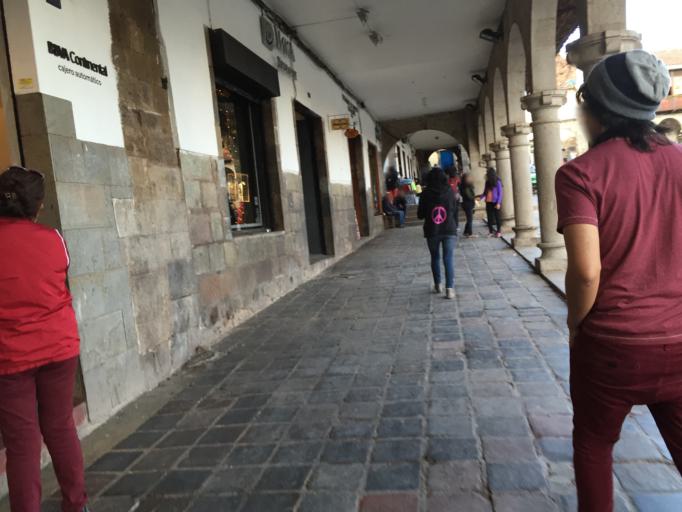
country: PE
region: Cusco
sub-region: Provincia de Cusco
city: Cusco
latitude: -13.5162
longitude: -71.9792
